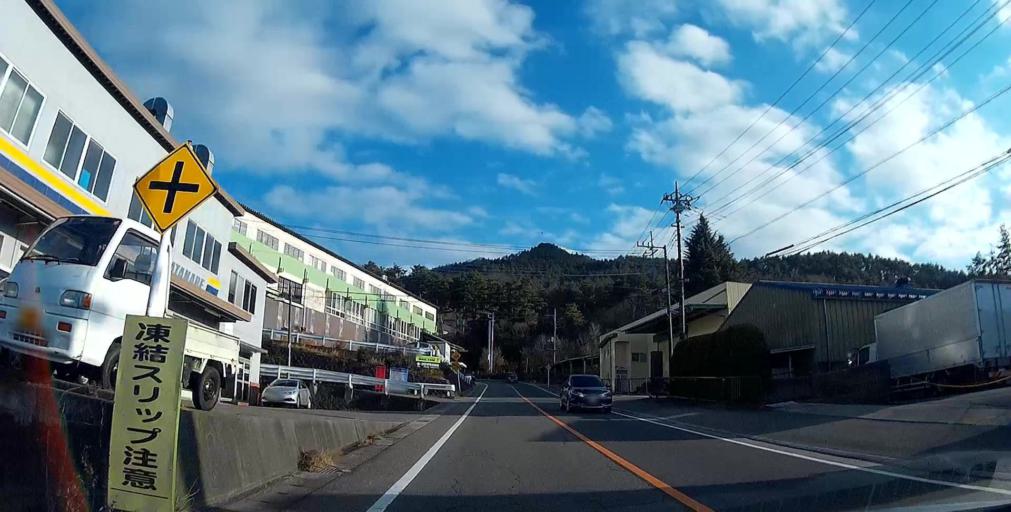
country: JP
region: Yamanashi
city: Fujikawaguchiko
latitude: 35.4769
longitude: 138.8169
